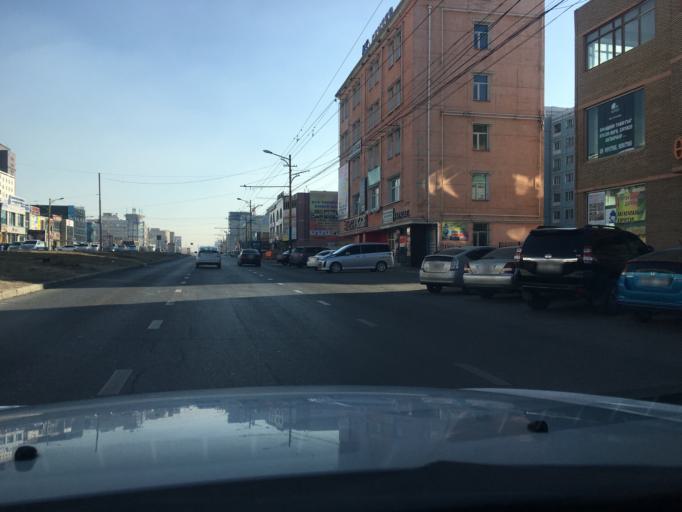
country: MN
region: Ulaanbaatar
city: Ulaanbaatar
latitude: 47.9224
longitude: 106.8704
